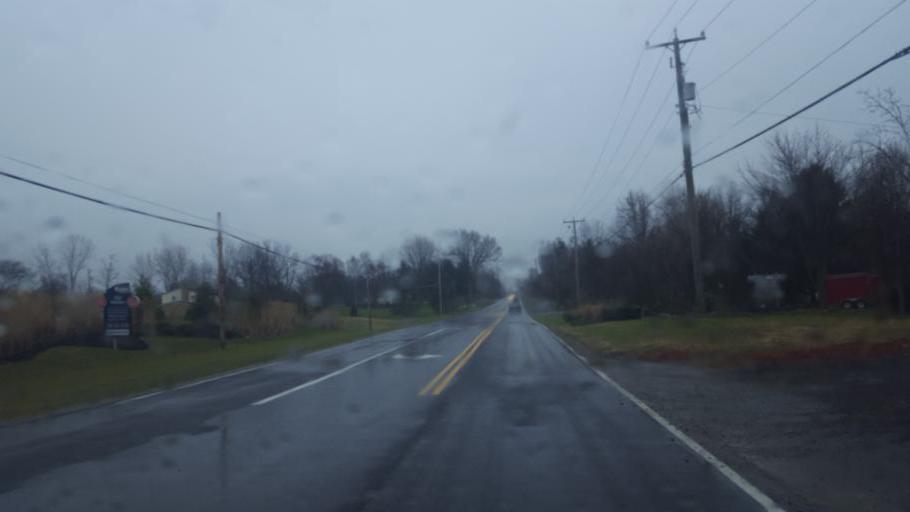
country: US
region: Ohio
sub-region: Delaware County
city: Lewis Center
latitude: 40.2210
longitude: -82.9833
